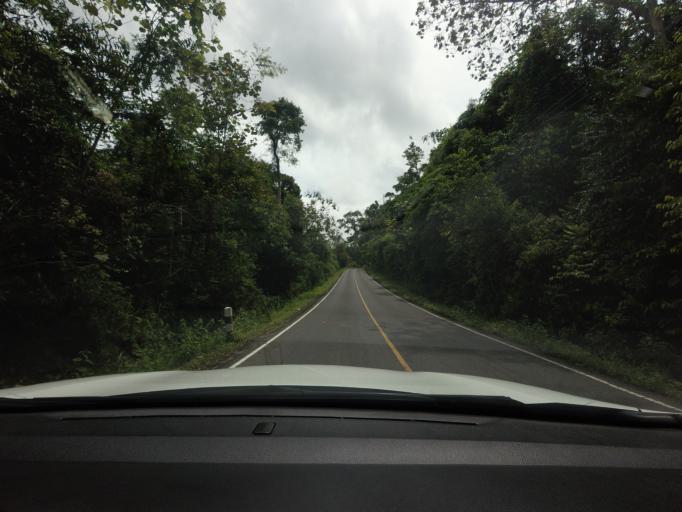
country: TH
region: Nakhon Nayok
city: Nakhon Nayok
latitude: 14.4219
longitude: 101.3711
